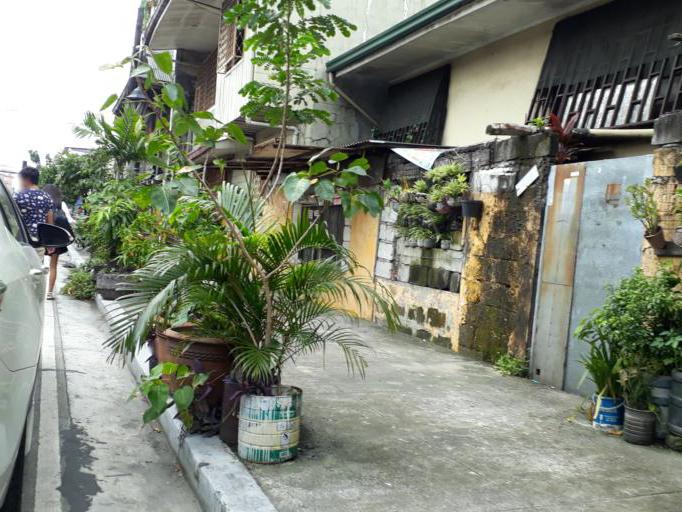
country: PH
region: Metro Manila
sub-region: City of Manila
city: Manila
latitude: 14.6149
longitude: 120.9975
